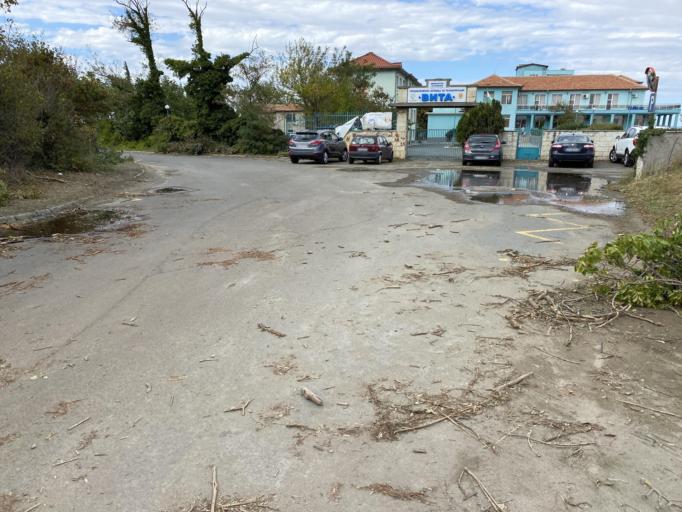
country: BG
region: Burgas
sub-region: Obshtina Pomorie
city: Pomorie
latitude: 42.5686
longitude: 27.6378
